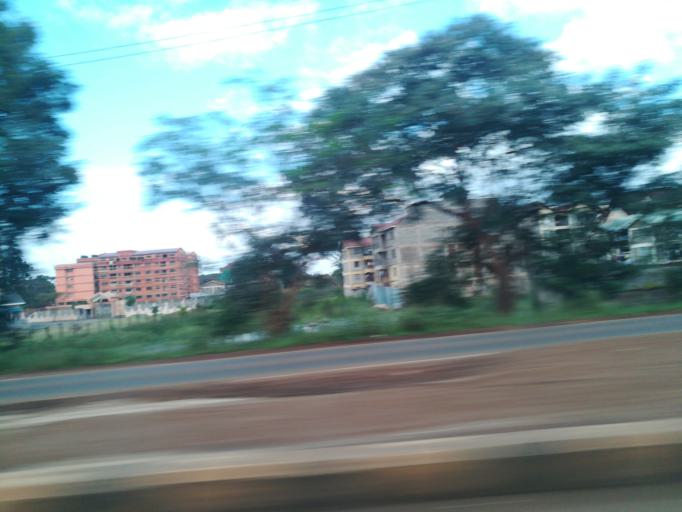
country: KE
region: Nairobi Area
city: Thika
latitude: -1.0381
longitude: 37.0635
